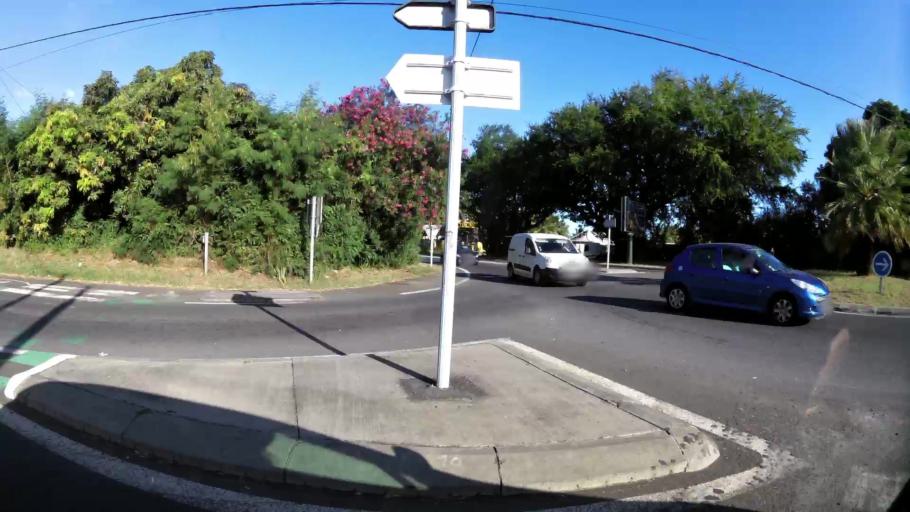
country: RE
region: Reunion
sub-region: Reunion
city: Saint-Louis
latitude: -21.2795
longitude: 55.3748
